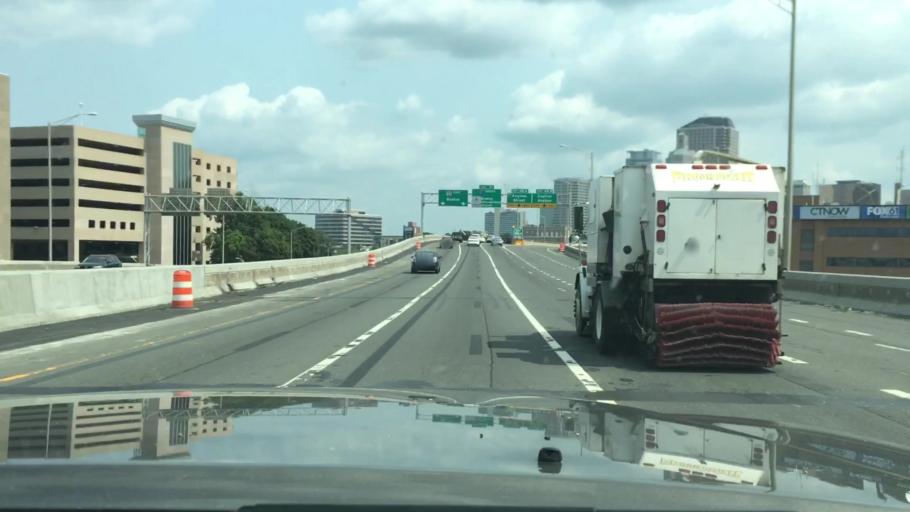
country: US
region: Connecticut
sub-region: Hartford County
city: Hartford
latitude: 41.7666
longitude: -72.6892
